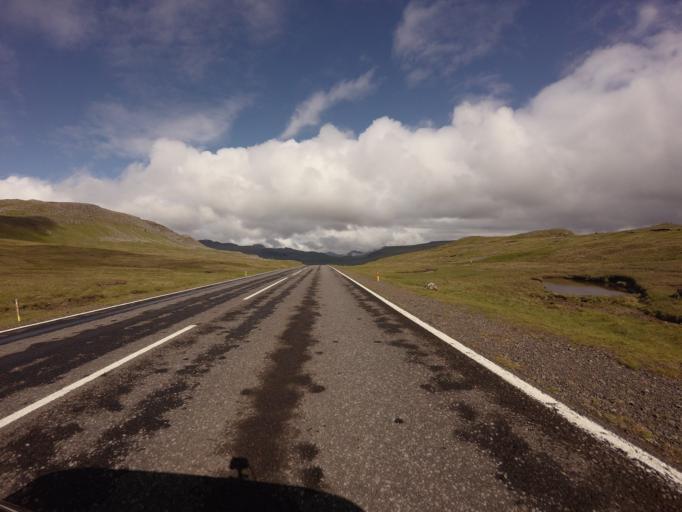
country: FO
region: Streymoy
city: Kollafjordhur
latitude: 62.0425
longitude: -6.8846
